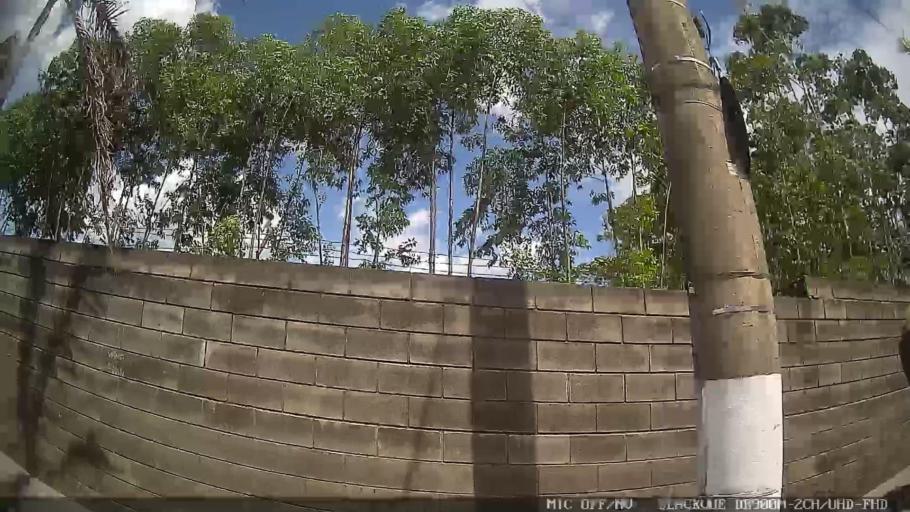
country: BR
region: Sao Paulo
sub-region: Conchas
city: Conchas
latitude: -23.0284
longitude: -48.0157
